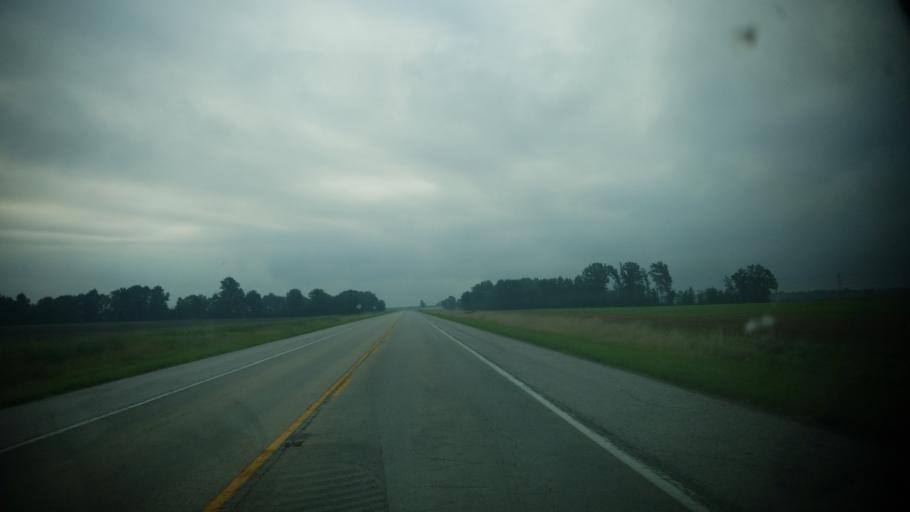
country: US
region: Illinois
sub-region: Clay County
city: Flora
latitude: 38.6757
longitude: -88.4286
